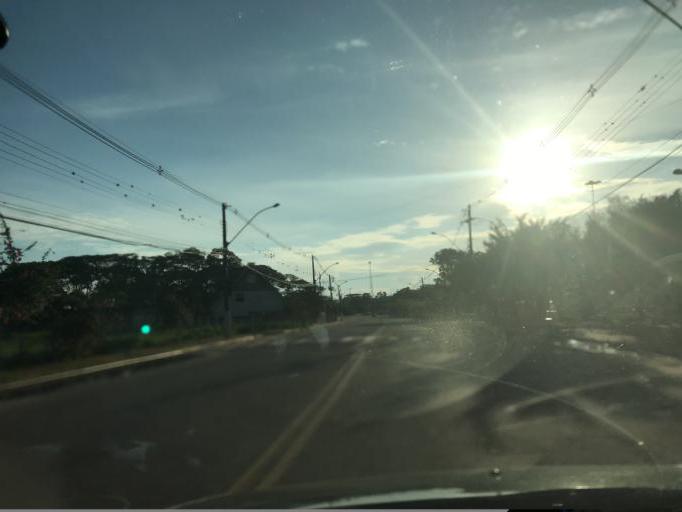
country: BR
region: Minas Gerais
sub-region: Tres Coracoes
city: Tres Coracoes
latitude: -21.7026
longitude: -45.2447
